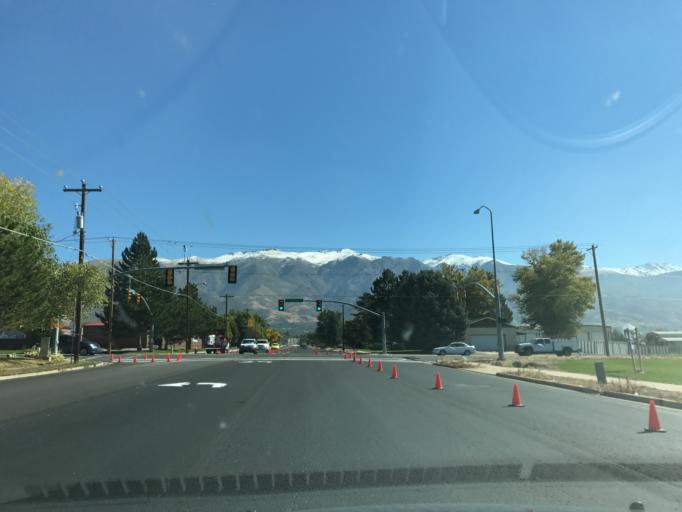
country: US
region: Utah
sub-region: Davis County
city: Hill Air Force Bace
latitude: 41.0889
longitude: -111.9509
